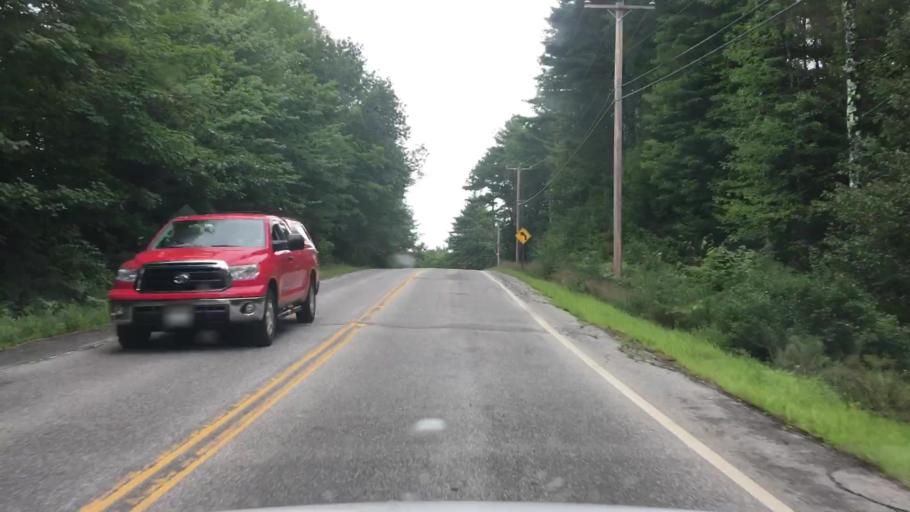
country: US
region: Maine
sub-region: York County
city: Cornish
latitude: 43.8184
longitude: -70.7735
